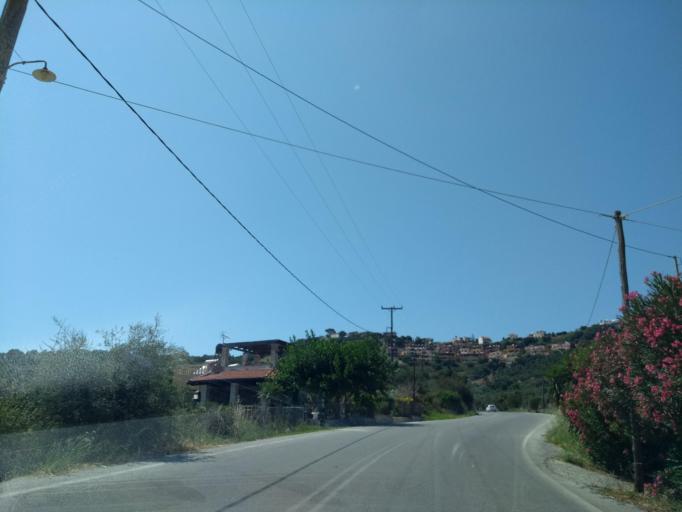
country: GR
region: Crete
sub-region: Nomos Chanias
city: Georgioupolis
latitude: 35.3696
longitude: 24.2474
